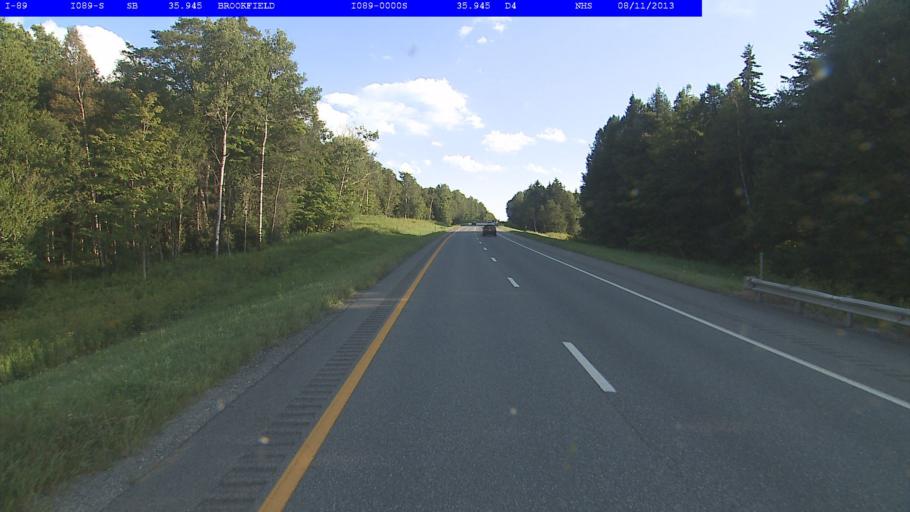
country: US
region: Vermont
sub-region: Orange County
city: Randolph
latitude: 44.0172
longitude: -72.6183
